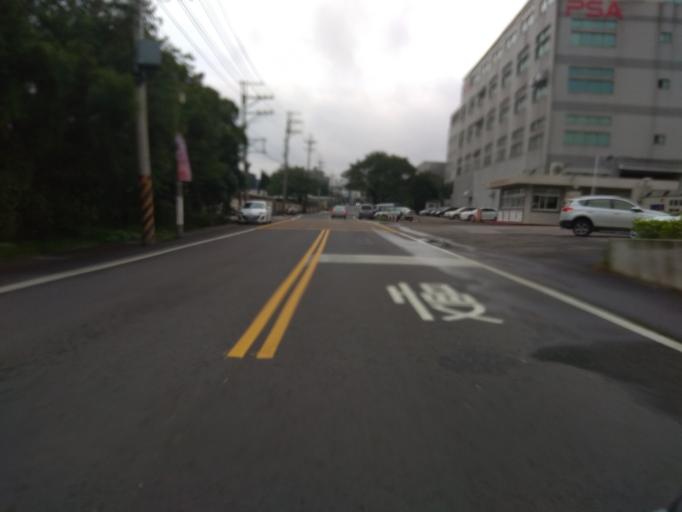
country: TW
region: Taiwan
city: Daxi
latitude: 24.9259
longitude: 121.1580
